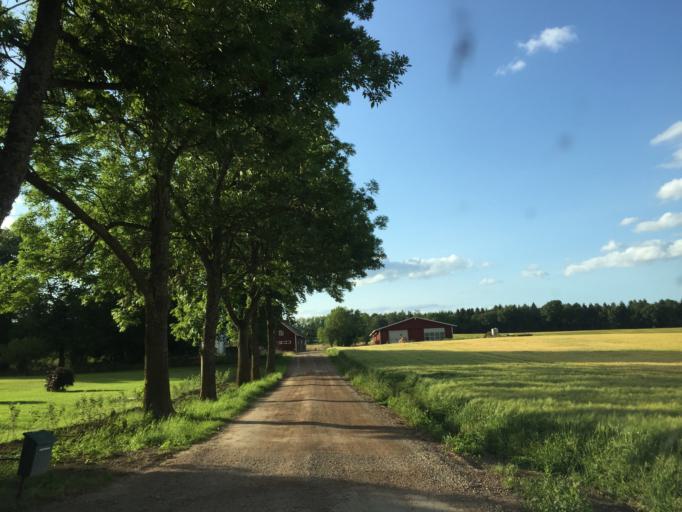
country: SE
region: OEstergoetland
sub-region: Vadstena Kommun
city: Vadstena
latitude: 58.4653
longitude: 14.8342
